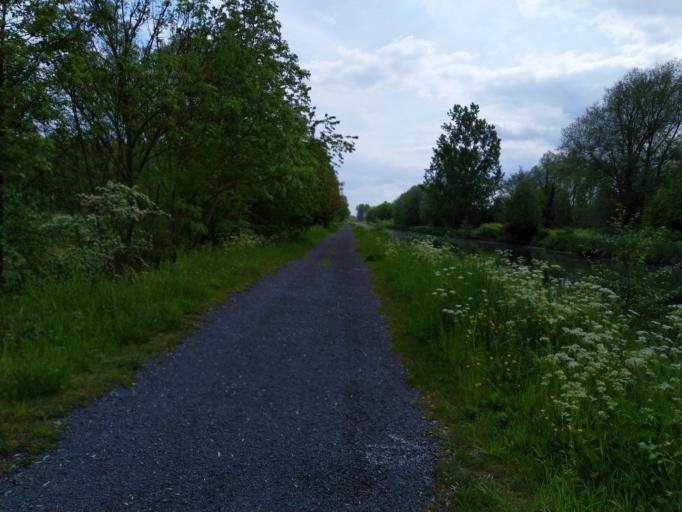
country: FR
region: Nord-Pas-de-Calais
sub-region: Departement du Nord
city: Landrecies
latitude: 50.0741
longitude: 3.6475
